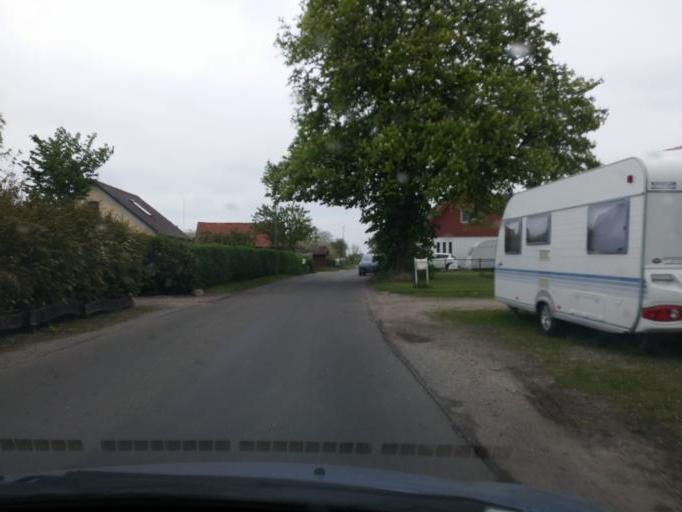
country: DK
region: South Denmark
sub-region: Odense Kommune
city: Bullerup
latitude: 55.4090
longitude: 10.5103
